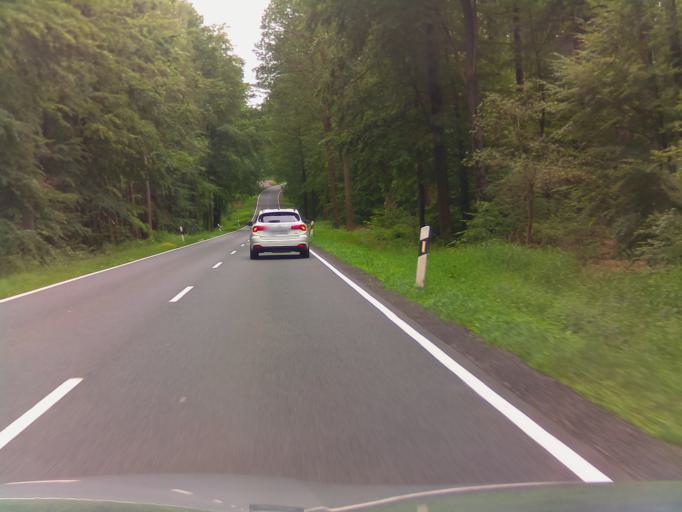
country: DE
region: Bavaria
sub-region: Regierungsbezirk Unterfranken
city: Rothenbuch
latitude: 49.9821
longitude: 9.3691
